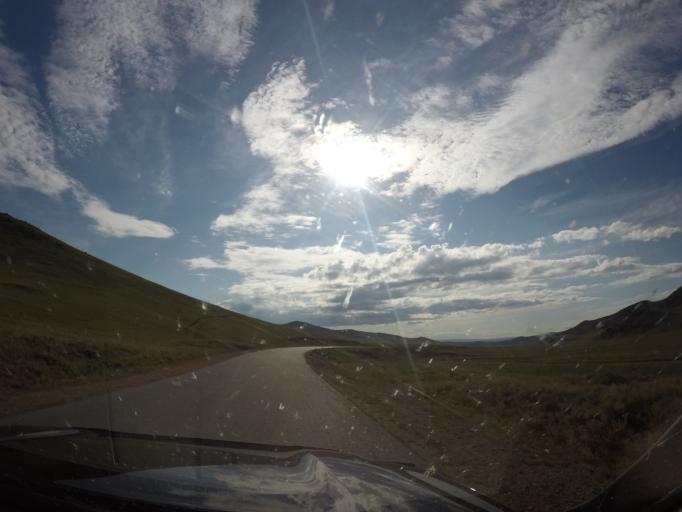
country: MN
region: Central Aimak
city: Bayandelger
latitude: 47.6938
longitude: 108.5395
